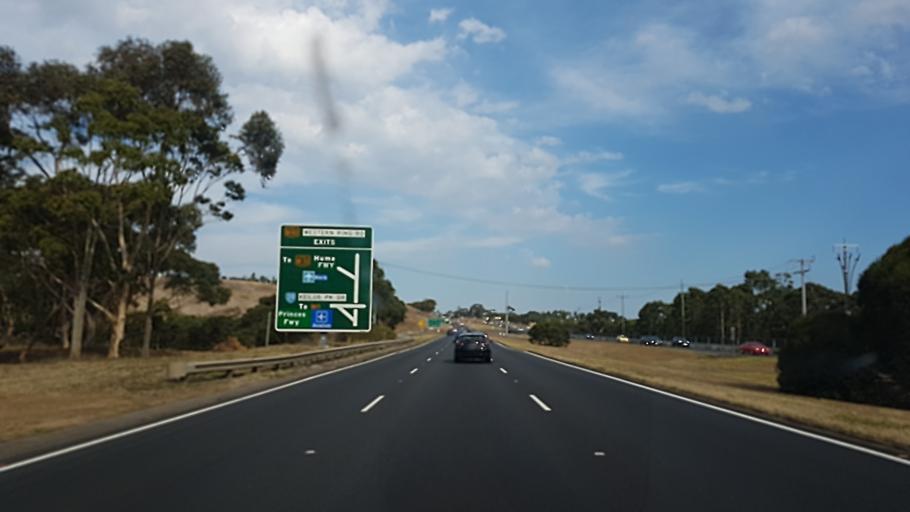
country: AU
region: Victoria
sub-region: Brimbank
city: Keilor
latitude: -37.7177
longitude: 144.8382
